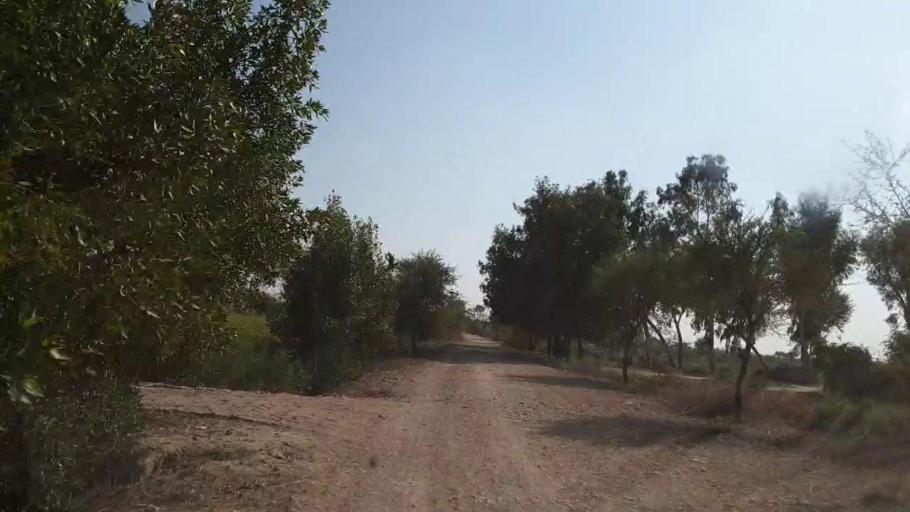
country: PK
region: Sindh
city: Mirpur Khas
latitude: 25.7205
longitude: 69.1613
